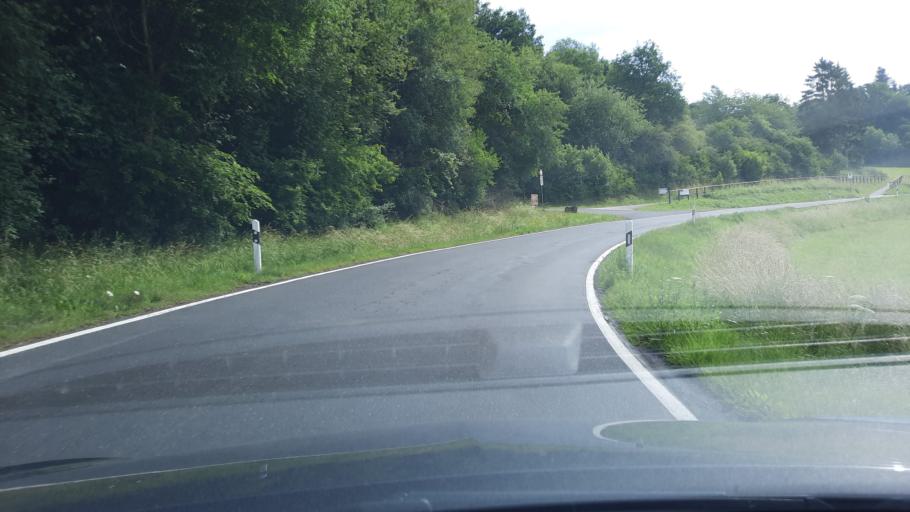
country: DE
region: Rheinland-Pfalz
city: Kempenich
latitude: 50.4122
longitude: 7.1308
